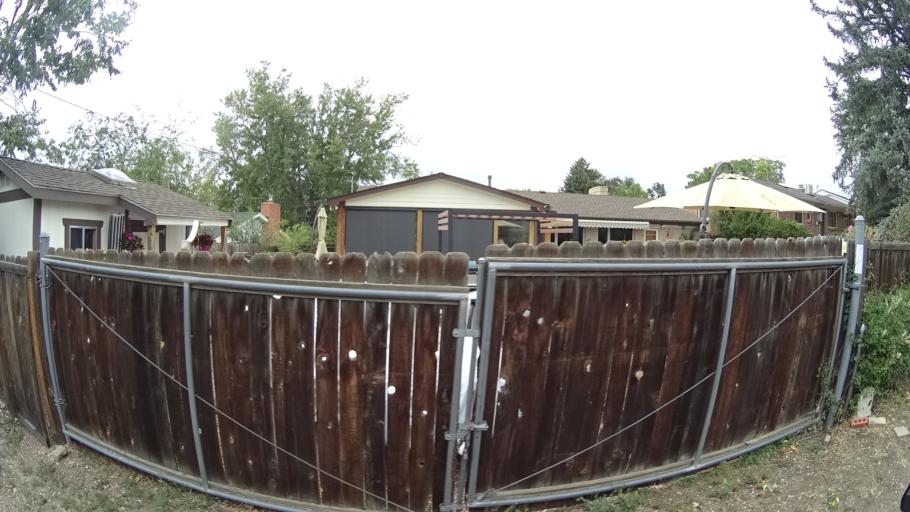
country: US
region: Colorado
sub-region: El Paso County
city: Colorado Springs
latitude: 38.8636
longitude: -104.7833
